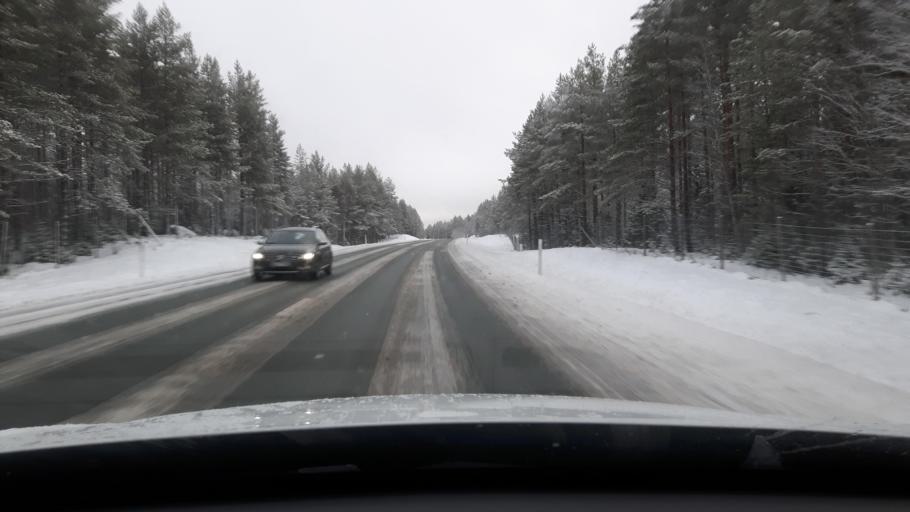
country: SE
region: Vaesterbotten
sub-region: Robertsfors Kommun
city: Robertsfors
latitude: 64.0367
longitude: 20.8433
